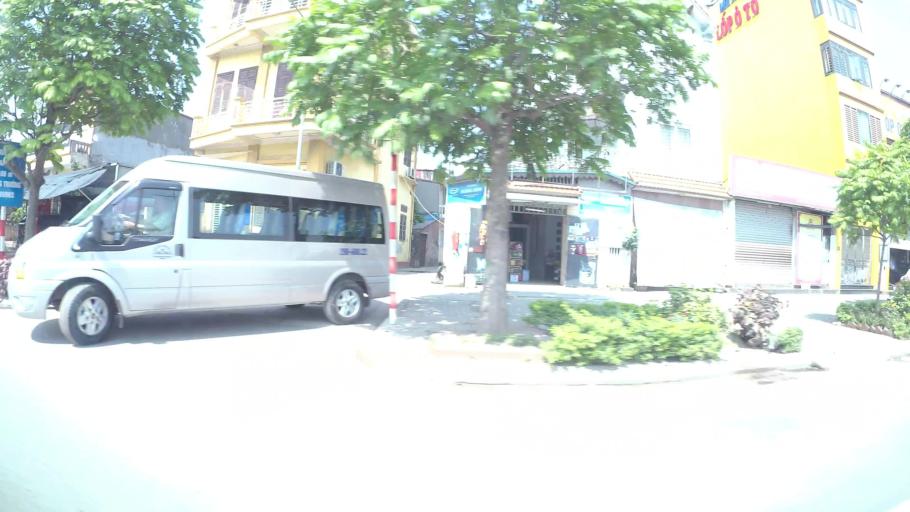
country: VN
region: Ha Noi
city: Hoan Kiem
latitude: 21.0630
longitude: 105.8815
